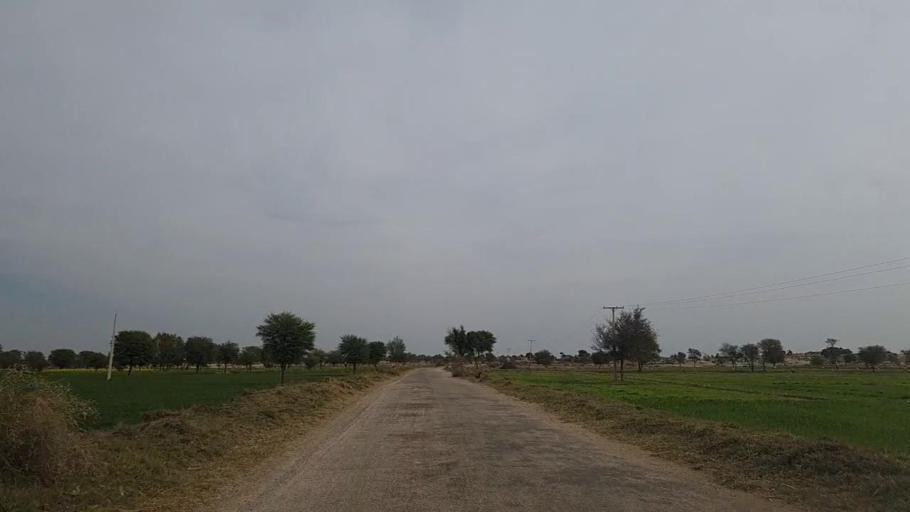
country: PK
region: Sindh
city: Jam Sahib
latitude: 26.4001
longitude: 68.5156
